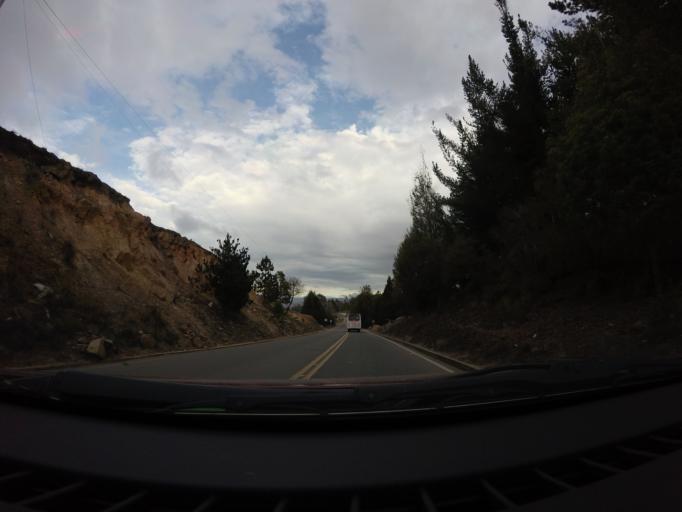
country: CO
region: Boyaca
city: Tunja
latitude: 5.5458
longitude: -73.3956
